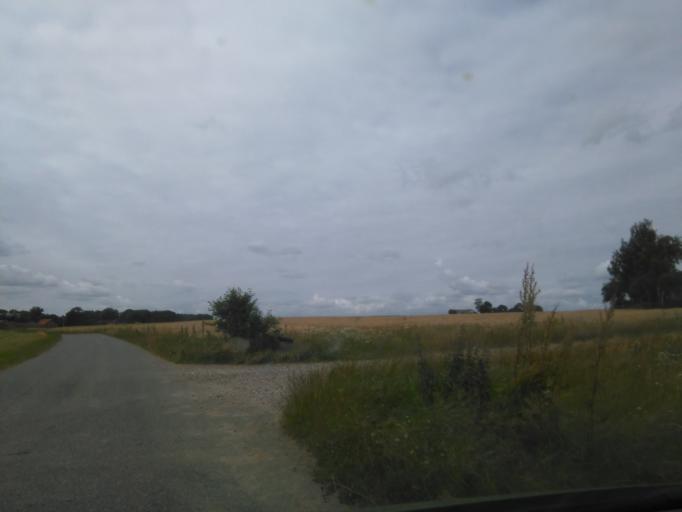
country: DK
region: Central Jutland
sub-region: Arhus Kommune
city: Solbjerg
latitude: 56.0126
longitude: 10.0659
